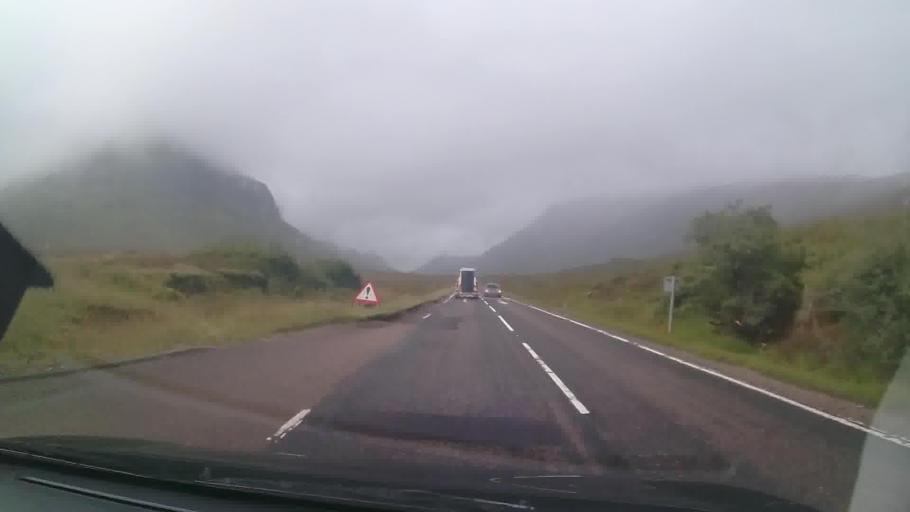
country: GB
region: Scotland
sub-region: Highland
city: Spean Bridge
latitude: 56.6612
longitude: -4.9180
